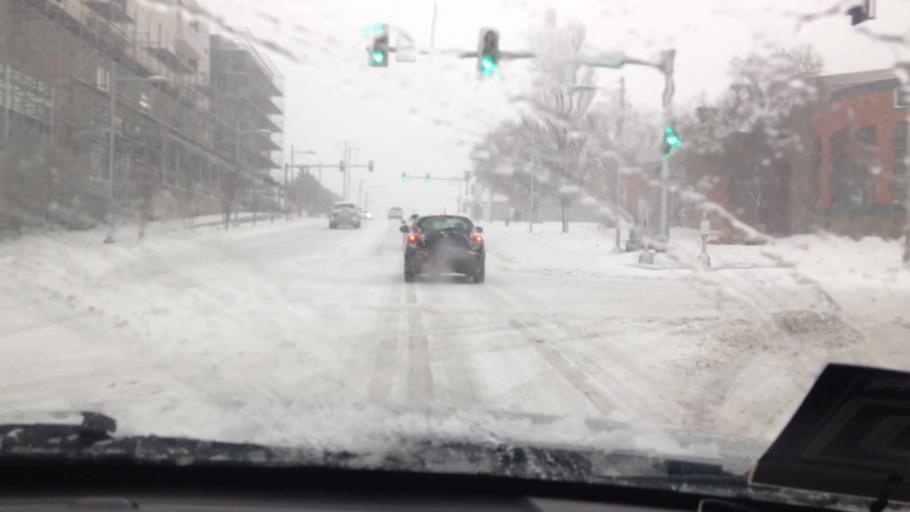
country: US
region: Kansas
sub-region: Johnson County
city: Westwood
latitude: 39.0442
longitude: -94.6120
